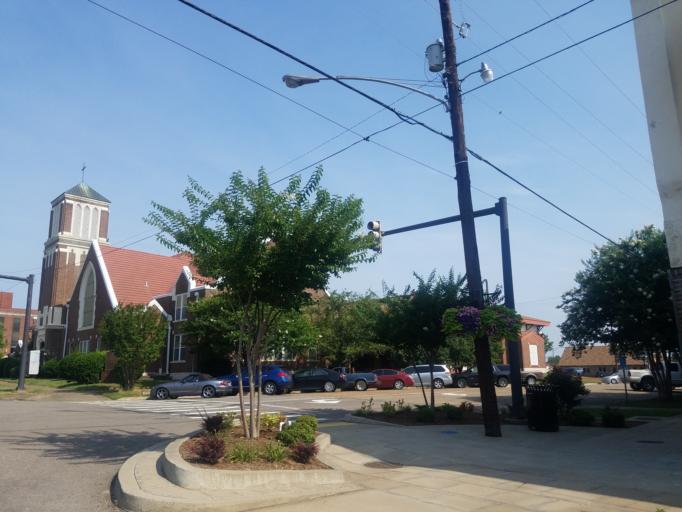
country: US
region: Arkansas
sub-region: Pope County
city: Russellville
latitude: 35.2787
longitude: -93.1358
